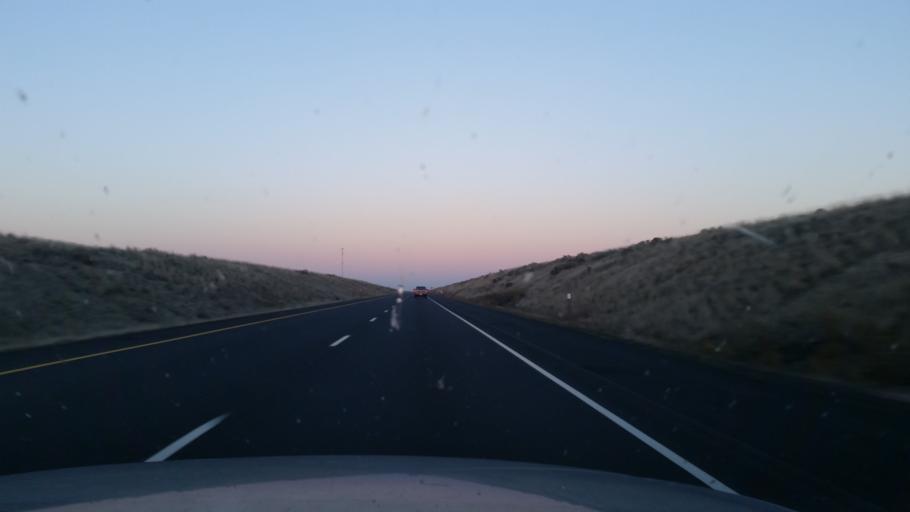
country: US
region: Washington
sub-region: Adams County
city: Ritzville
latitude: 47.0902
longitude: -118.7036
